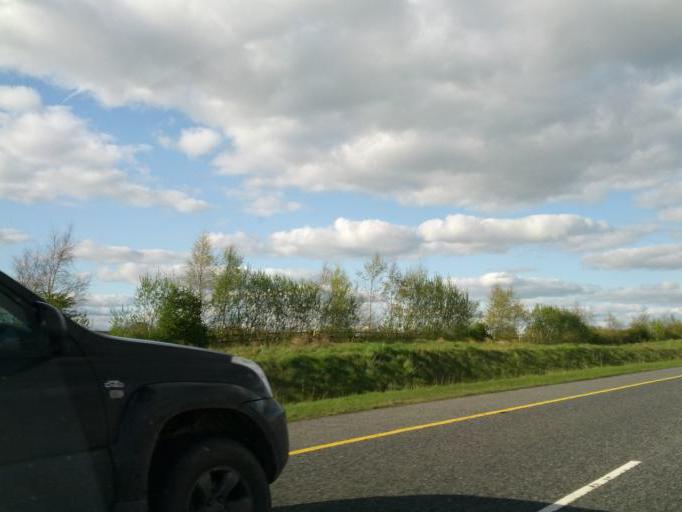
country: IE
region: Leinster
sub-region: An Iarmhi
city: Rochfortbridge
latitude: 53.4401
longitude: -7.2088
